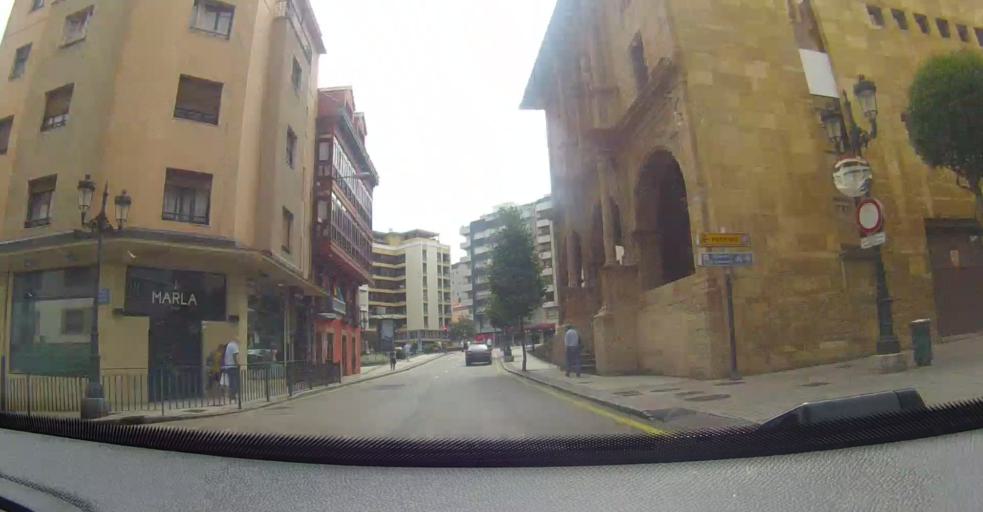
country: ES
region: Asturias
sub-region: Province of Asturias
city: Oviedo
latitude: 43.3640
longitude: -5.8476
